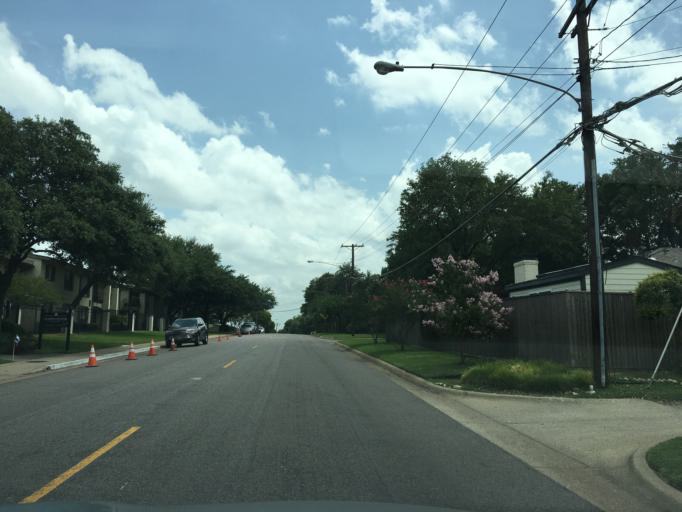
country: US
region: Texas
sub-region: Dallas County
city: University Park
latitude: 32.8879
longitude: -96.7751
